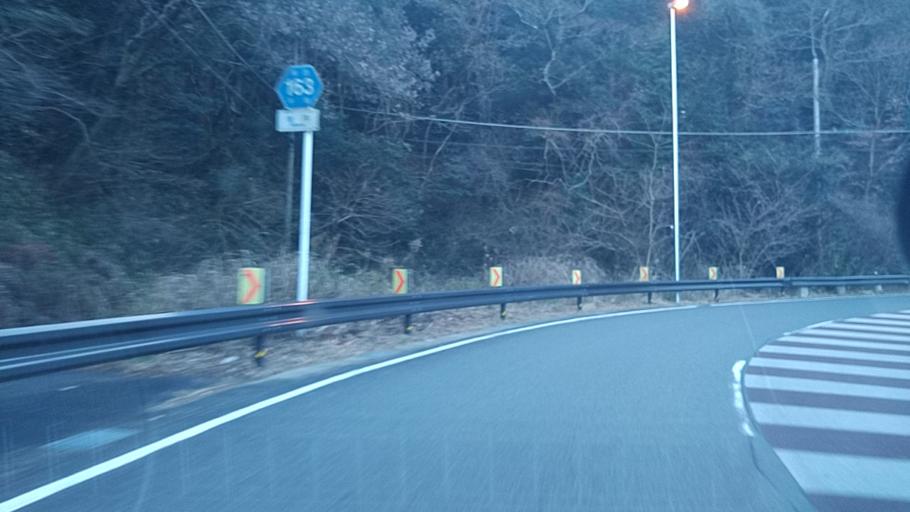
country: JP
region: Chiba
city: Kimitsu
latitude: 35.2637
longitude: 139.9316
